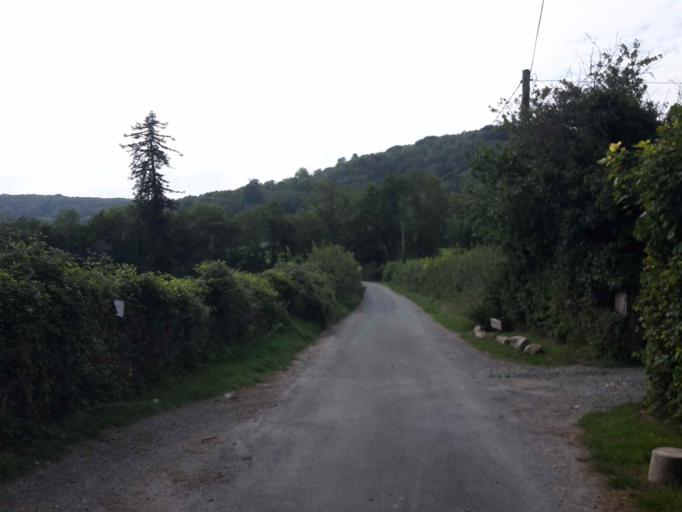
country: GB
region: England
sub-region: West Sussex
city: Washington
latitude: 50.9002
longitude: -0.3721
